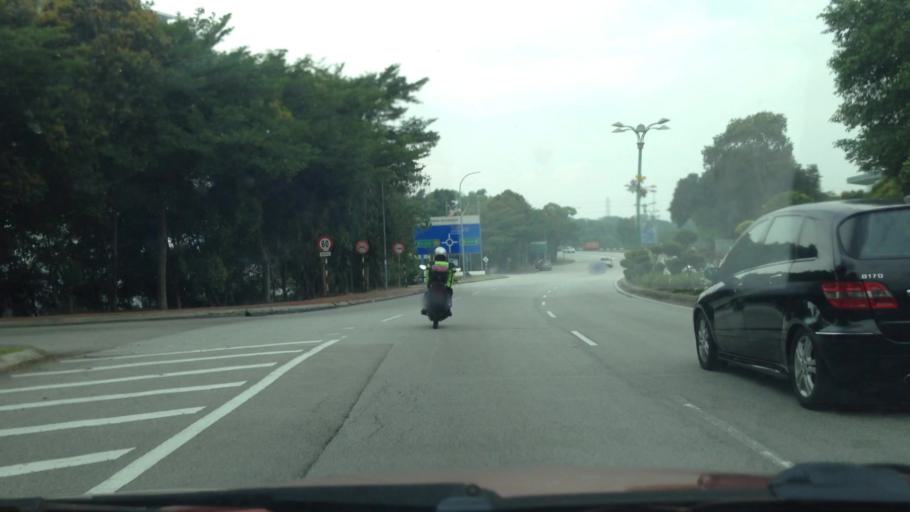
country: MY
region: Selangor
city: Shah Alam
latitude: 3.0724
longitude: 101.5374
